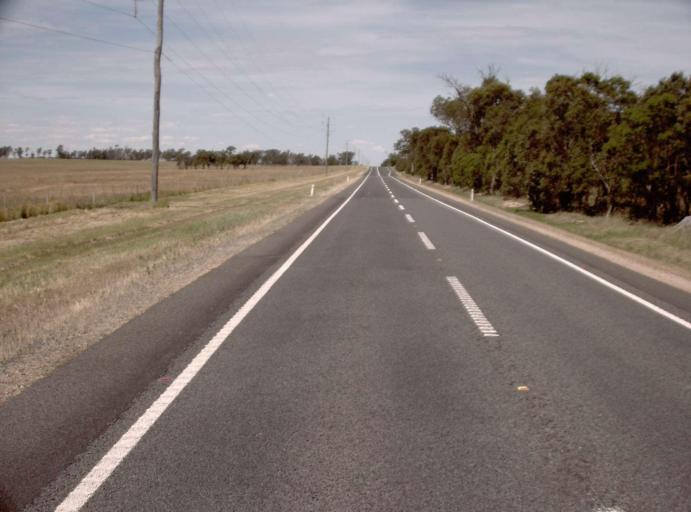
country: AU
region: Victoria
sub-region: East Gippsland
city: Bairnsdale
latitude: -37.8929
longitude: 147.3786
